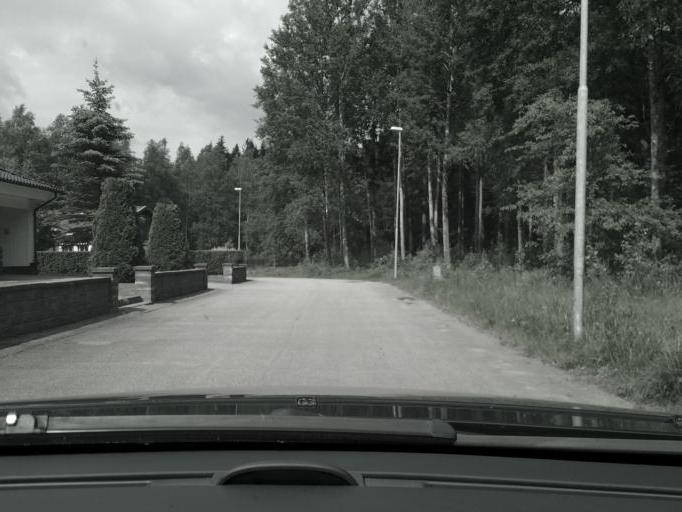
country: SE
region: Kronoberg
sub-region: Vaxjo Kommun
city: Lammhult
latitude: 57.1707
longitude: 14.6072
